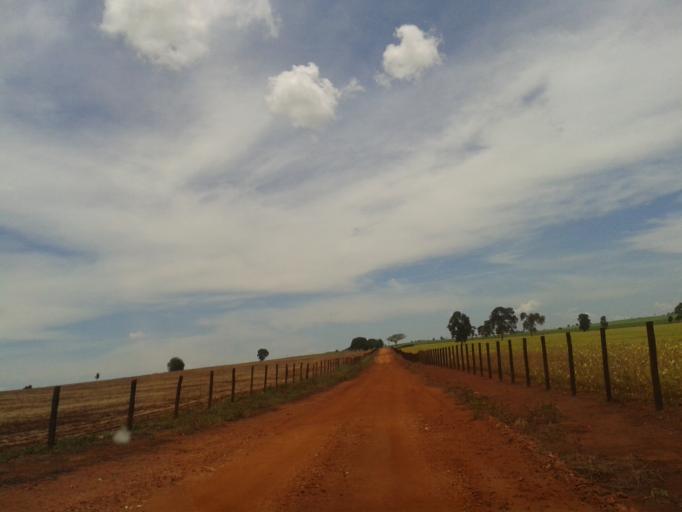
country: BR
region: Minas Gerais
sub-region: Capinopolis
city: Capinopolis
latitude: -18.7031
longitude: -49.7125
